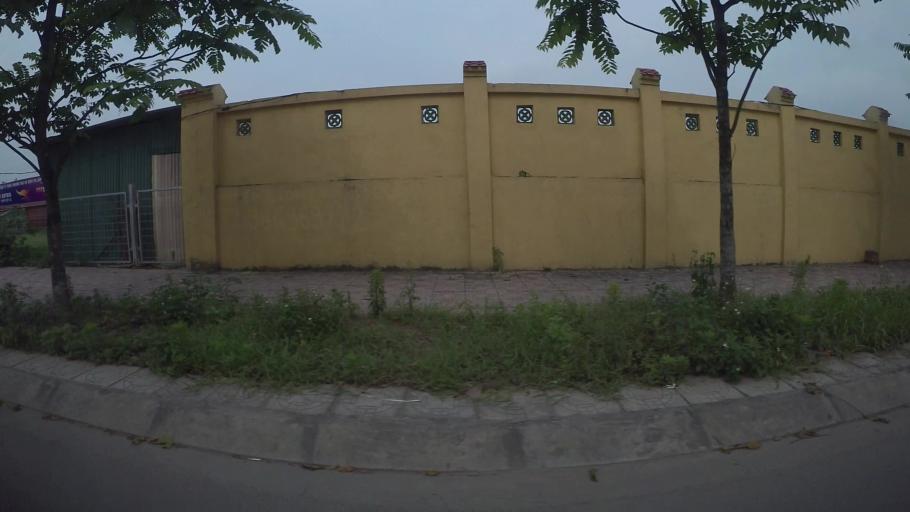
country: VN
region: Ha Noi
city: Trau Quy
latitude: 21.0562
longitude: 105.9032
